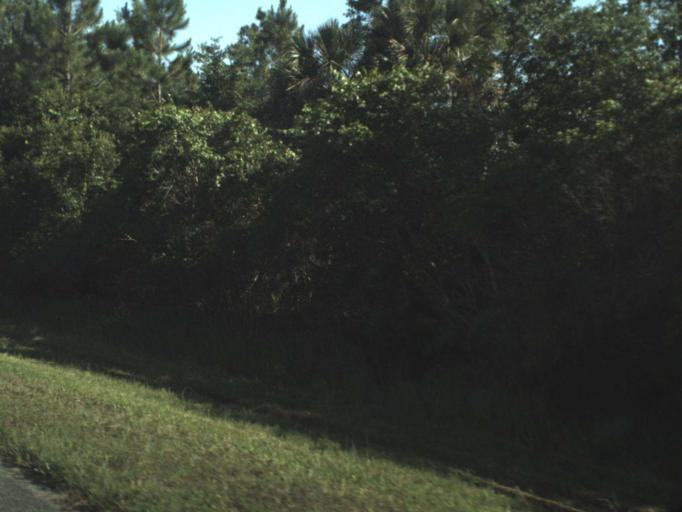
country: US
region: Florida
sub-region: Brevard County
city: Mims
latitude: 28.6784
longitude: -80.9807
